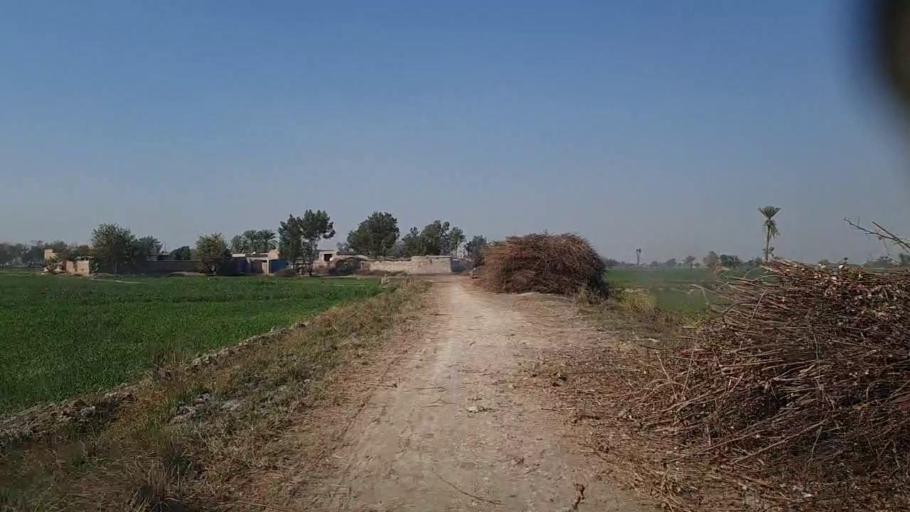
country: PK
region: Sindh
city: Khairpur
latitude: 28.0235
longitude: 69.7391
